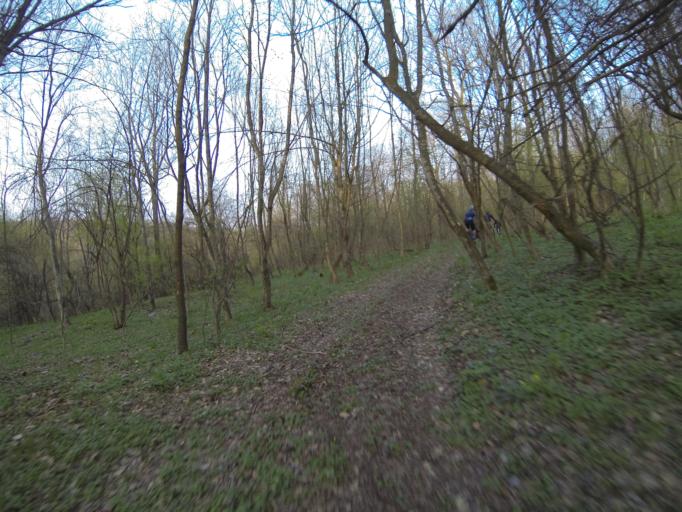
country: RO
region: Dolj
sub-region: Comuna Bucovat
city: Bucovat
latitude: 44.2749
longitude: 23.7538
